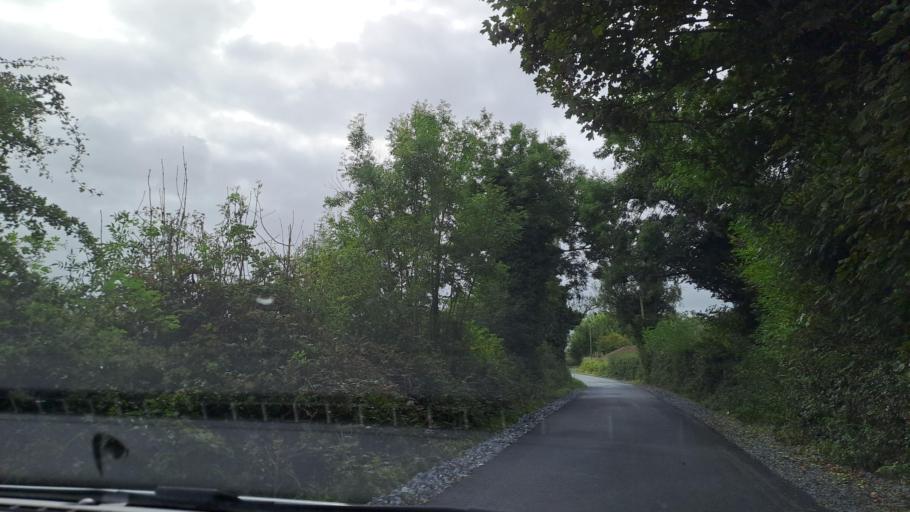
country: IE
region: Ulster
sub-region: County Monaghan
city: Carrickmacross
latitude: 53.9869
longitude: -6.7767
